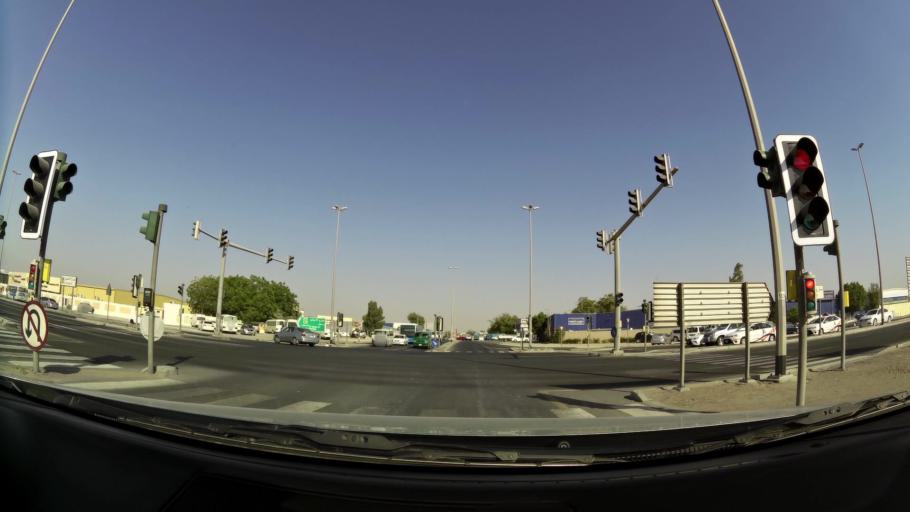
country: AE
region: Dubai
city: Dubai
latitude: 25.1207
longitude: 55.2248
